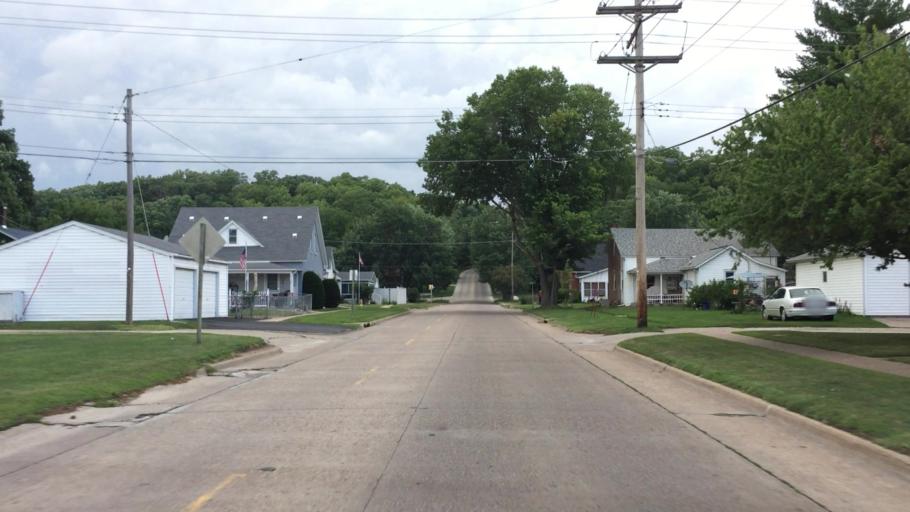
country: US
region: Iowa
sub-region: Lee County
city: Fort Madison
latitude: 40.6345
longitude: -91.3246
